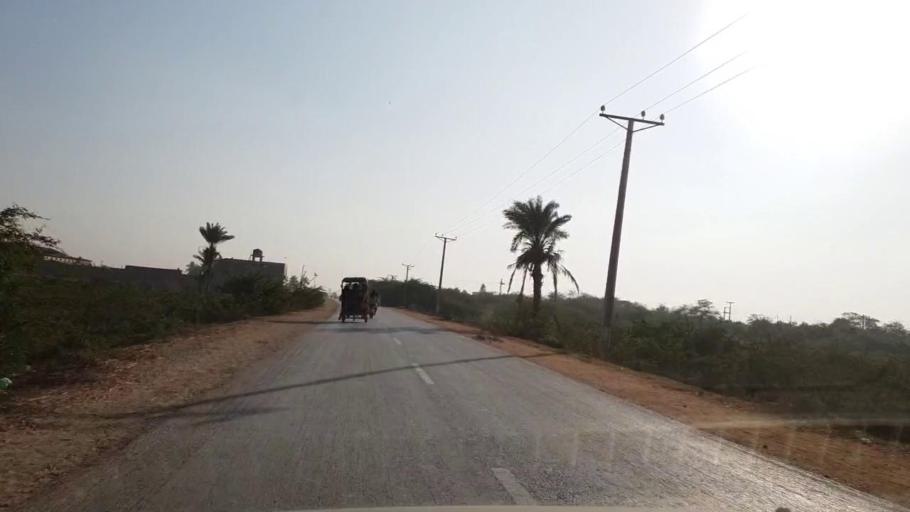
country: PK
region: Sindh
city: Bulri
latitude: 24.8578
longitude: 68.3288
